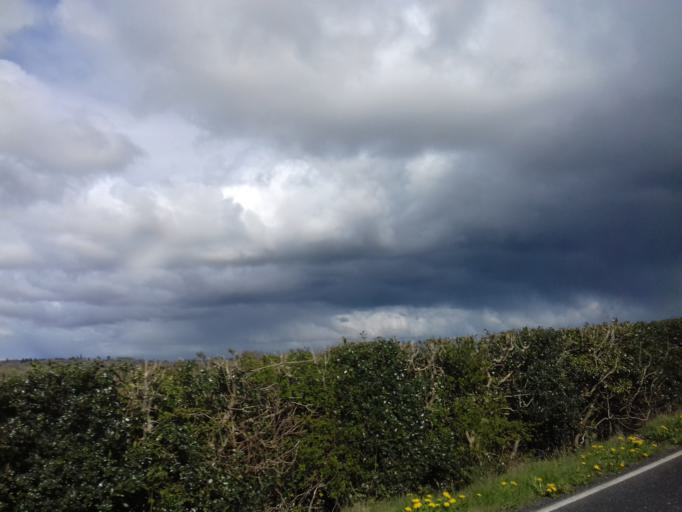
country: IE
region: Ulster
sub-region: County Donegal
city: Ballyshannon
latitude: 54.4689
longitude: -8.0525
